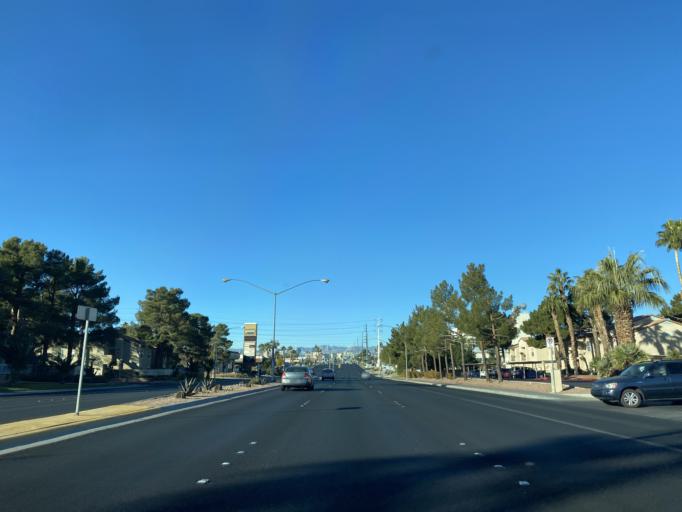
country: US
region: Nevada
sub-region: Clark County
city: Winchester
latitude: 36.1152
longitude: -115.1060
